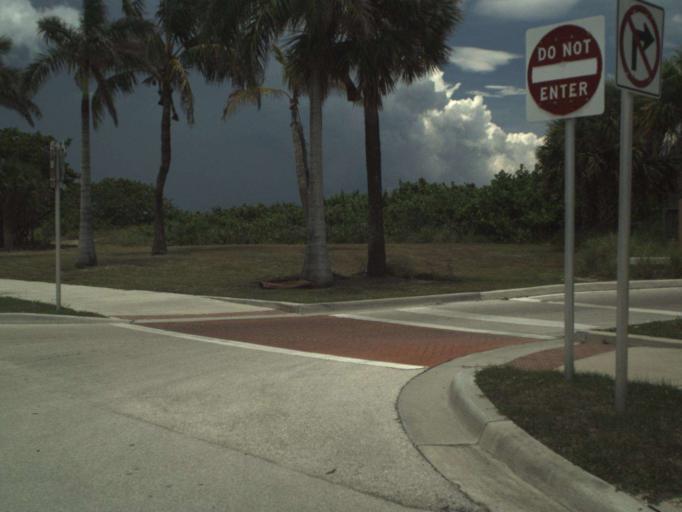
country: US
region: Florida
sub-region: Saint Lucie County
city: Fort Pierce
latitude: 27.4600
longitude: -80.2885
